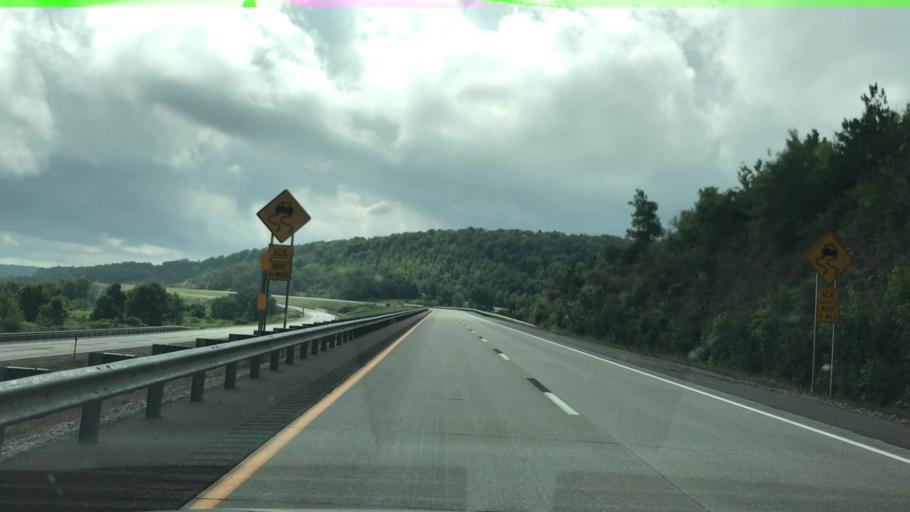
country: US
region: New York
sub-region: Steuben County
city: Wayland
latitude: 42.5178
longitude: -77.5409
